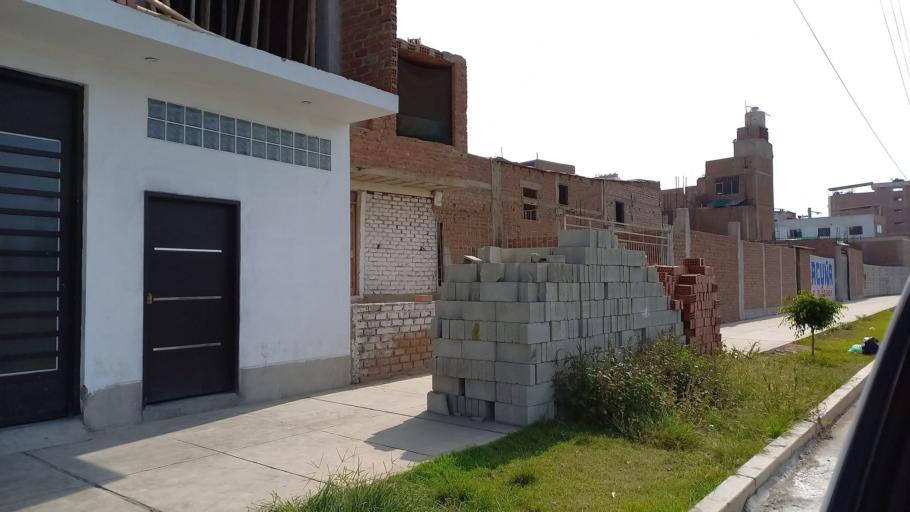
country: PE
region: La Libertad
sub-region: Provincia de Trujillo
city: La Esperanza
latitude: -8.1013
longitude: -79.0538
